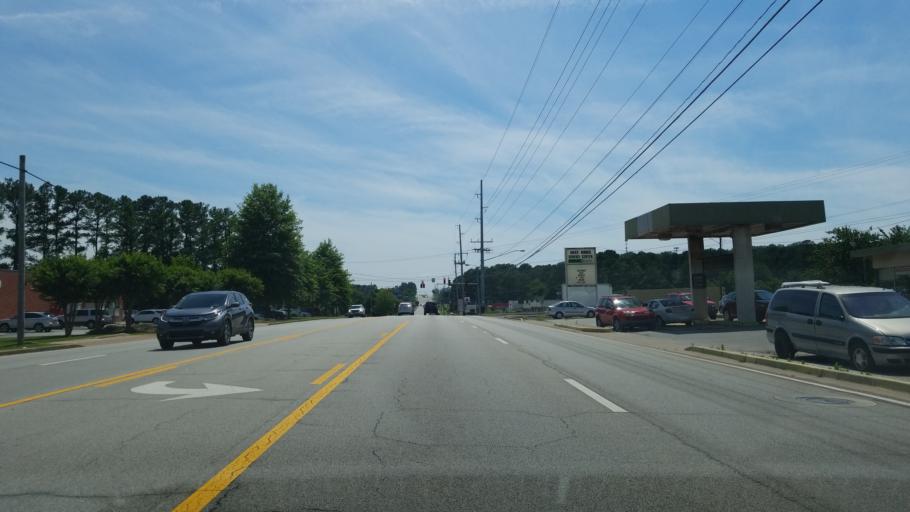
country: US
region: Tennessee
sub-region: Hamilton County
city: East Brainerd
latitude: 35.0414
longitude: -85.1681
